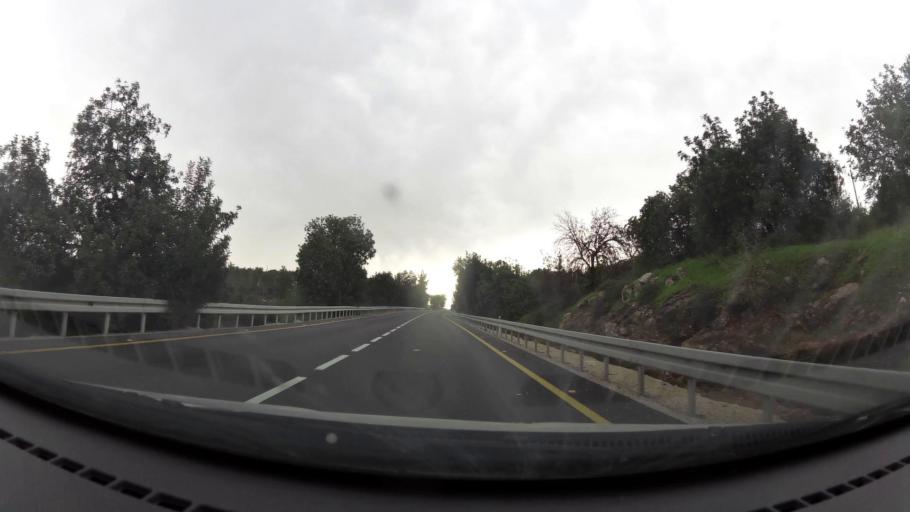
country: PS
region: West Bank
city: Surif
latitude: 31.6728
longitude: 35.0167
